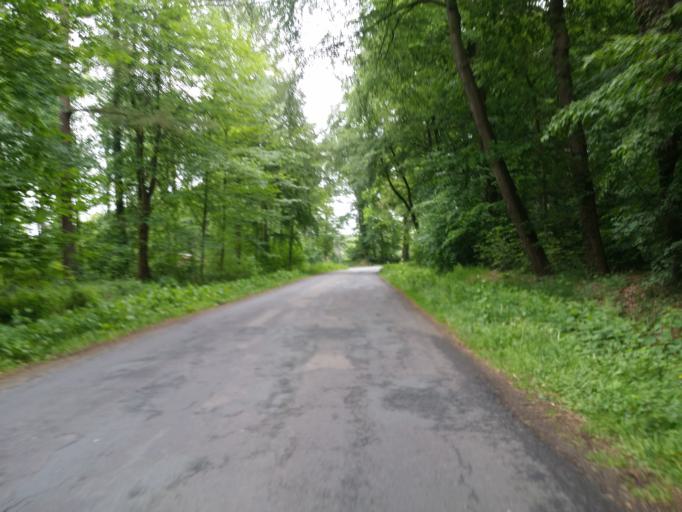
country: DE
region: Lower Saxony
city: Rastede
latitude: 53.2395
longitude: 8.2186
